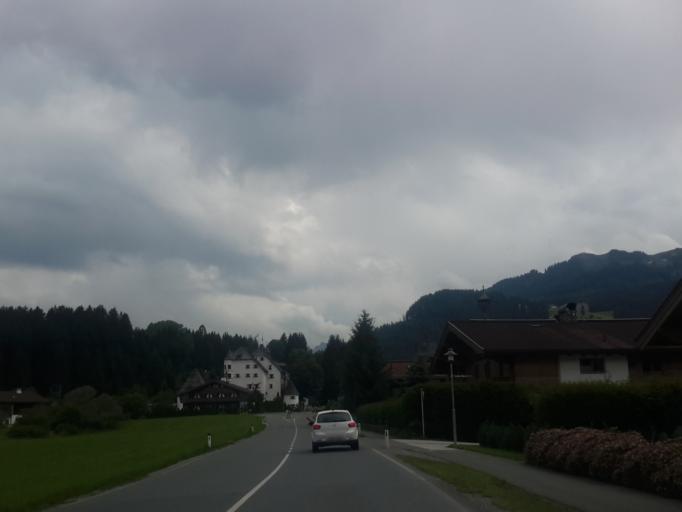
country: AT
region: Tyrol
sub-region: Politischer Bezirk Kitzbuhel
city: Reith bei Kitzbuhel
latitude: 47.4671
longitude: 12.3501
